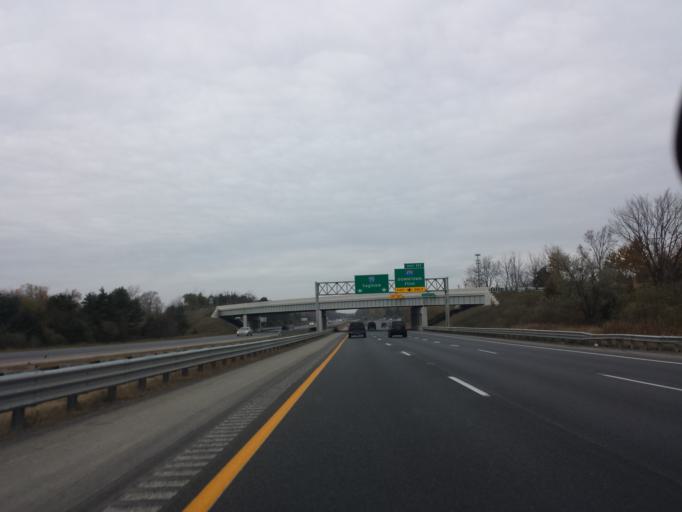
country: US
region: Michigan
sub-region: Genesee County
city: Grand Blanc
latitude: 42.9143
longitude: -83.6717
